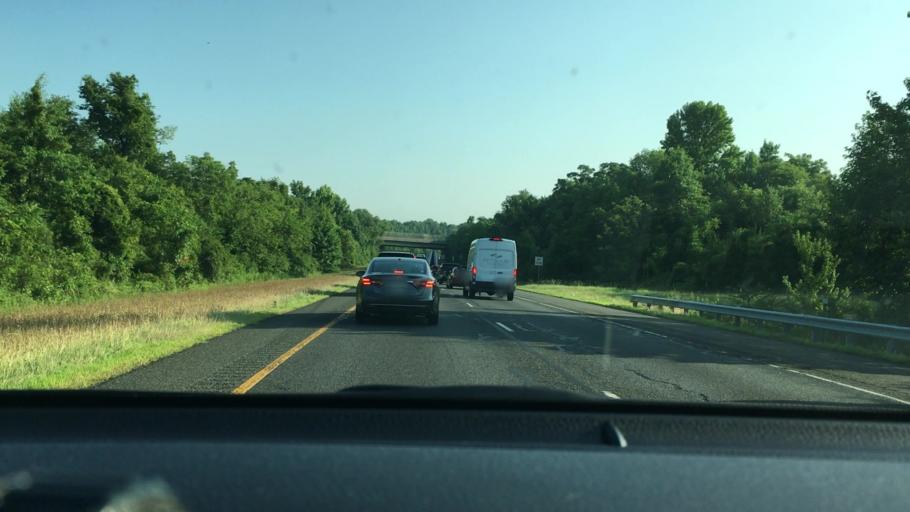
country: US
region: New Jersey
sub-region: Camden County
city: Glendora
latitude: 39.8289
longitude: -75.1039
